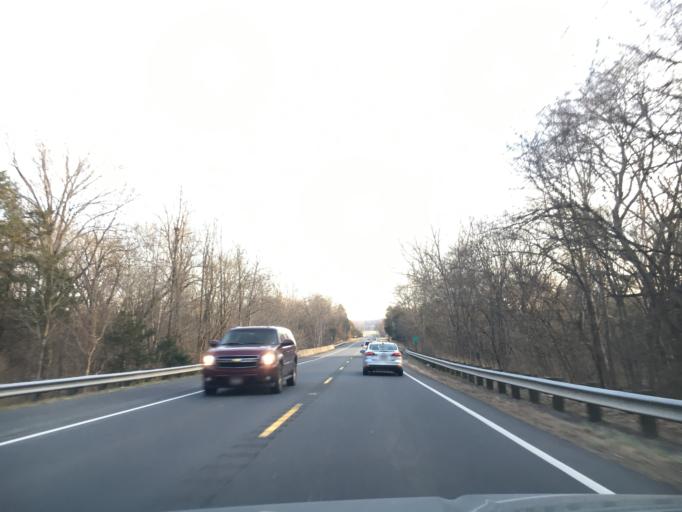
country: US
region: Virginia
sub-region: Culpeper County
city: Culpeper
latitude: 38.3645
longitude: -77.9761
